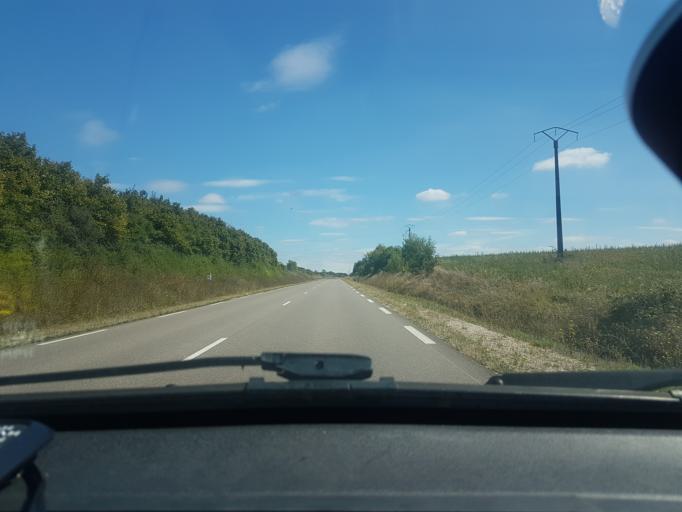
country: FR
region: Franche-Comte
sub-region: Departement de la Haute-Saone
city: Gray-la-Ville
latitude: 47.4050
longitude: 5.4813
